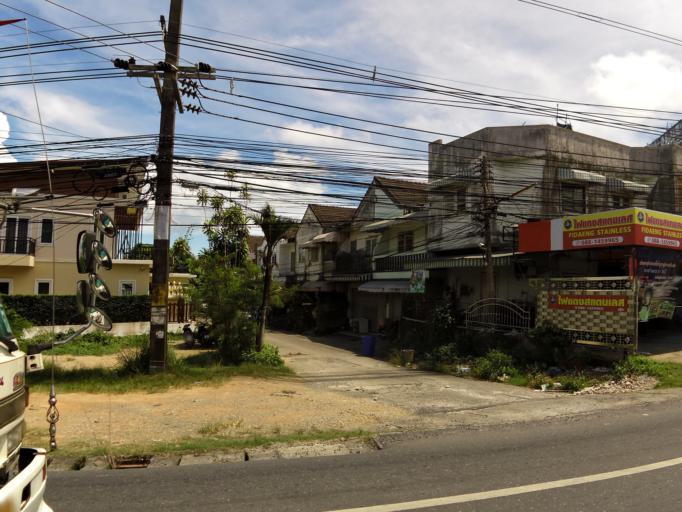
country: TH
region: Phuket
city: Mueang Phuket
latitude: 7.8654
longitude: 98.3487
